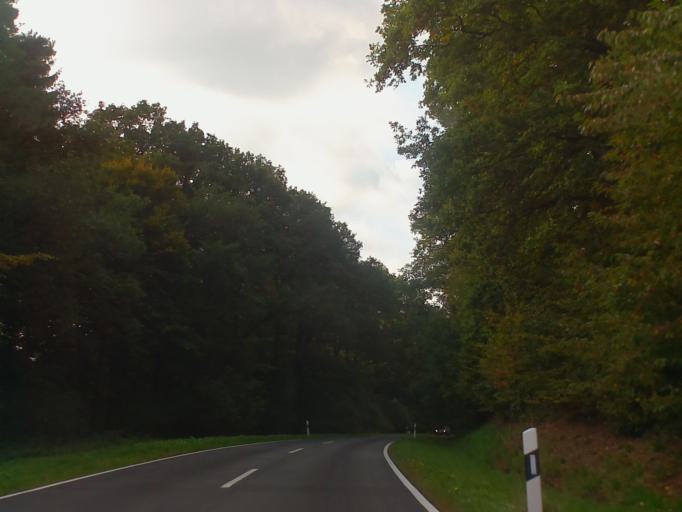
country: DE
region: Thuringia
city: Grossensee
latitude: 50.9482
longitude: 9.9800
